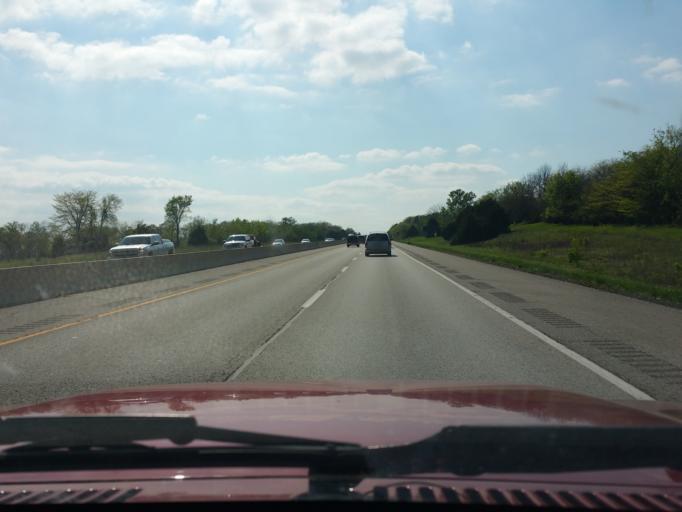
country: US
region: Kansas
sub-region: Douglas County
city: Lawrence
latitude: 38.9978
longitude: -95.3028
